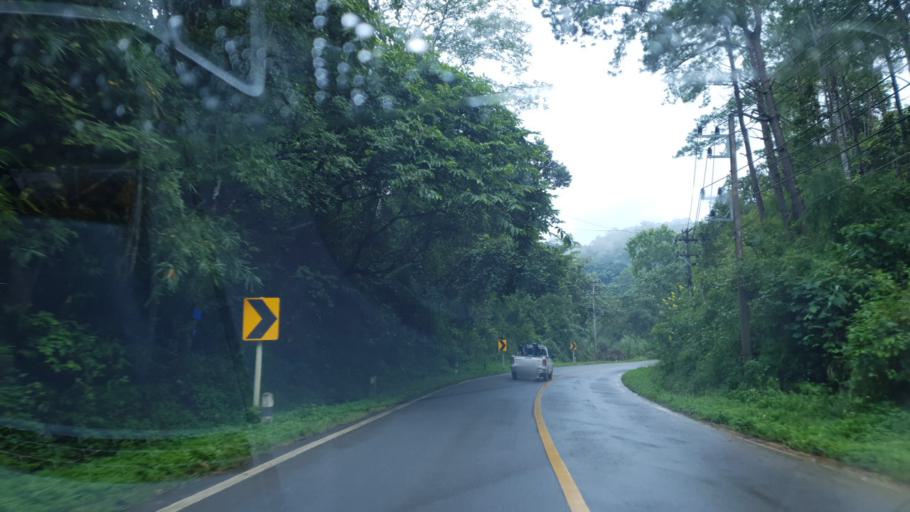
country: TH
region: Mae Hong Son
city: Ban Huai I Huak
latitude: 18.1611
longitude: 98.0425
